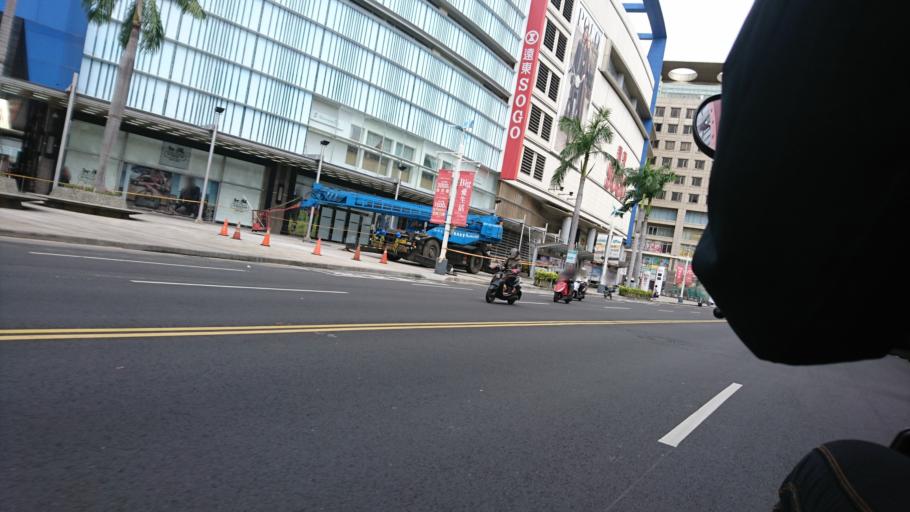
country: TW
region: Taiwan
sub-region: Hsinchu
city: Hsinchu
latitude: 24.8090
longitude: 120.9749
